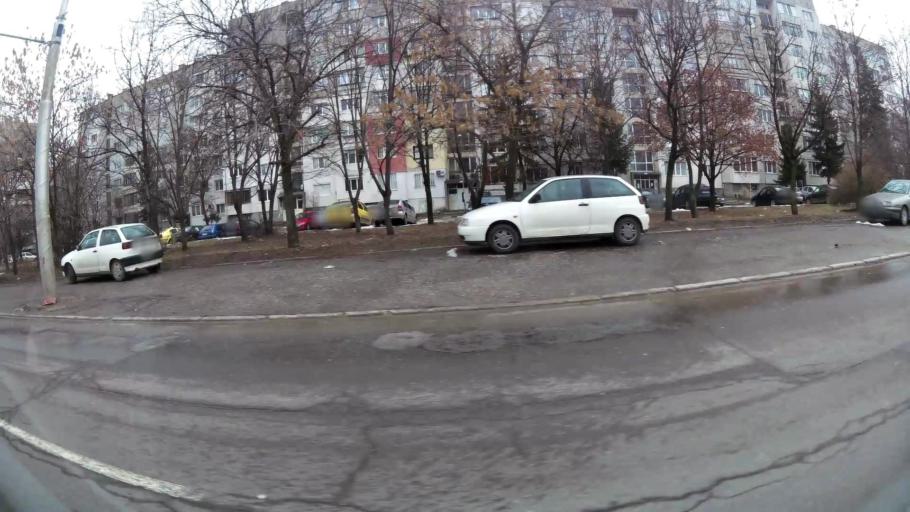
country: BG
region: Sofiya
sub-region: Obshtina Bozhurishte
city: Bozhurishte
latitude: 42.7269
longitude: 23.2454
